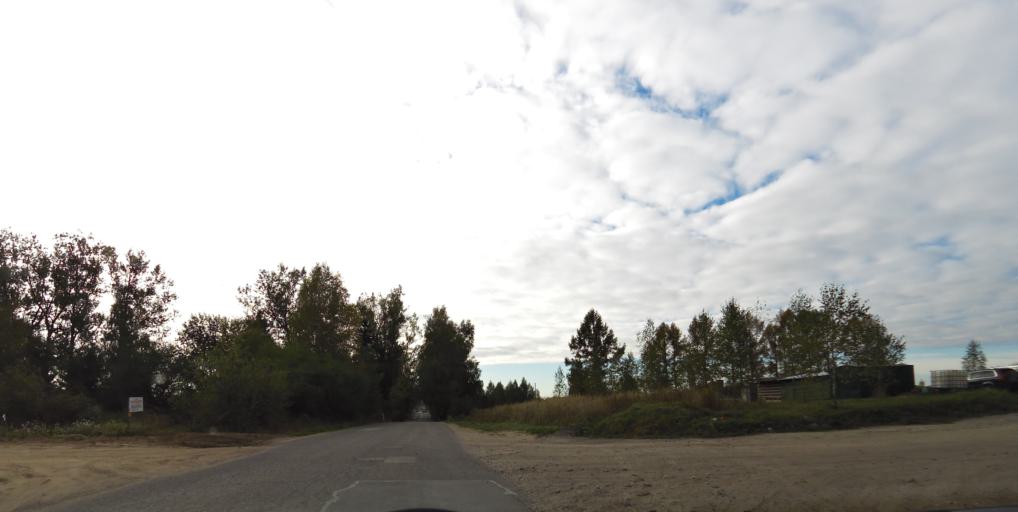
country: LT
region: Vilnius County
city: Pilaite
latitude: 54.7167
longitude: 25.1592
